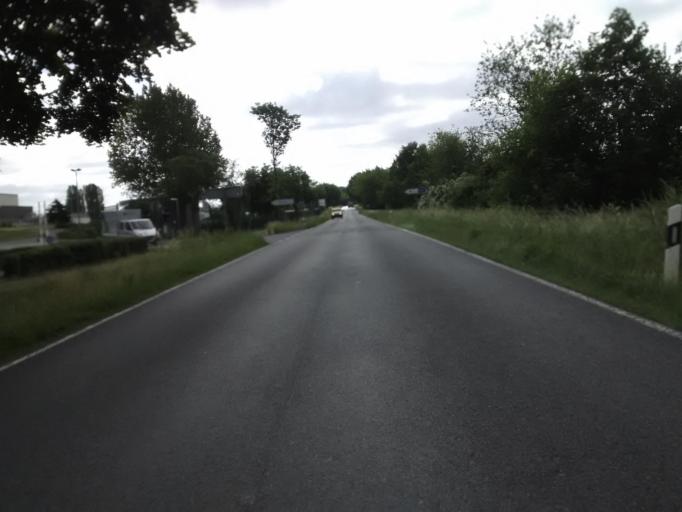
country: DE
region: Berlin
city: Blankenfelde
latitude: 52.6609
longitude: 13.4144
